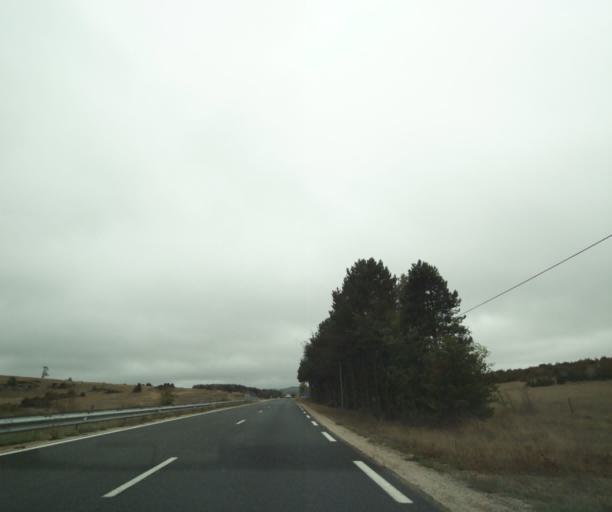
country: FR
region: Midi-Pyrenees
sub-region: Departement de l'Aveyron
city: La Cavalerie
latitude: 44.0352
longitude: 3.1471
